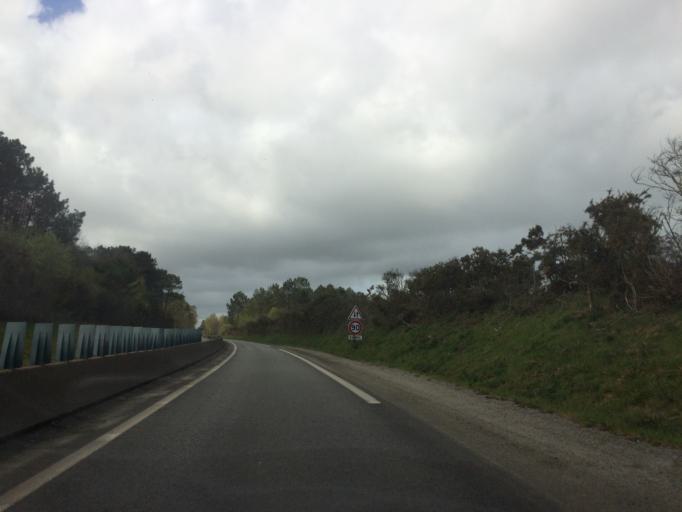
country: FR
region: Brittany
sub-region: Departement du Morbihan
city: Pluherlin
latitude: 47.6746
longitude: -2.3666
